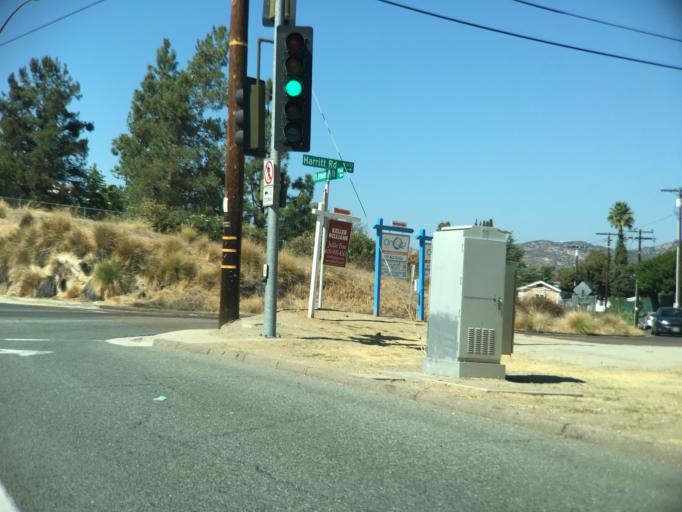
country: US
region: California
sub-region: San Diego County
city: Lakeside
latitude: 32.8475
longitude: -116.8833
